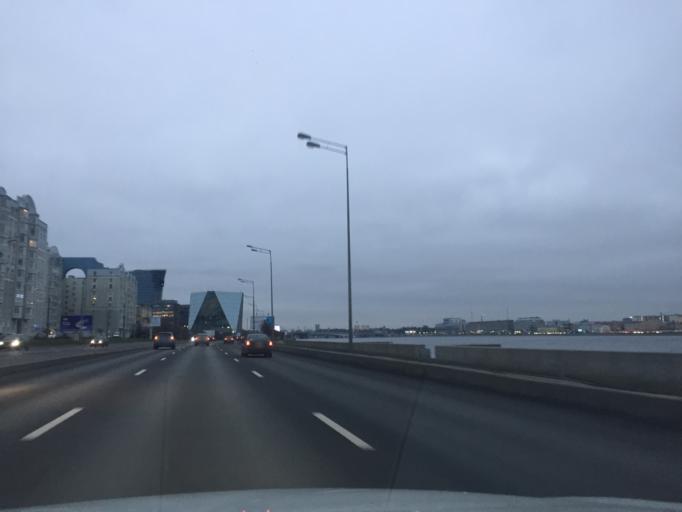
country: RU
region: St.-Petersburg
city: Centralniy
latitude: 59.9389
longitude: 30.4035
